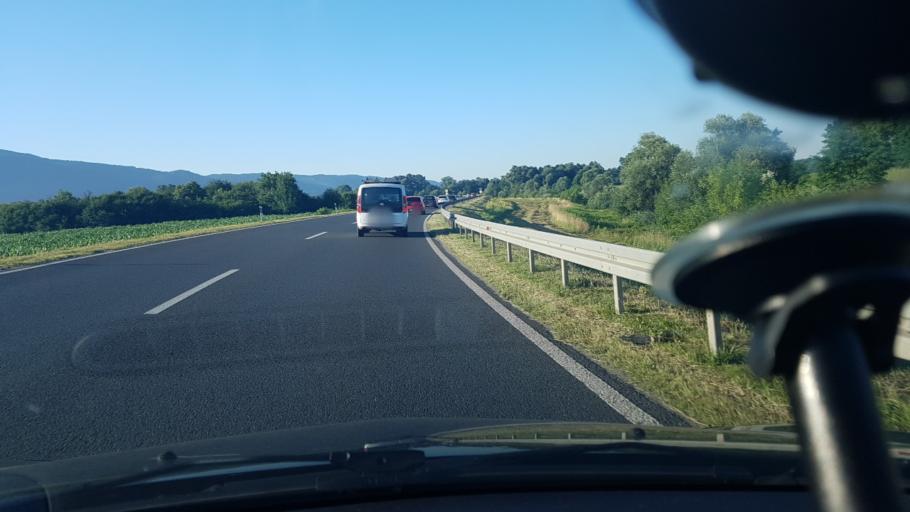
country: HR
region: Zagrebacka
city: Pojatno
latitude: 45.9000
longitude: 15.8160
